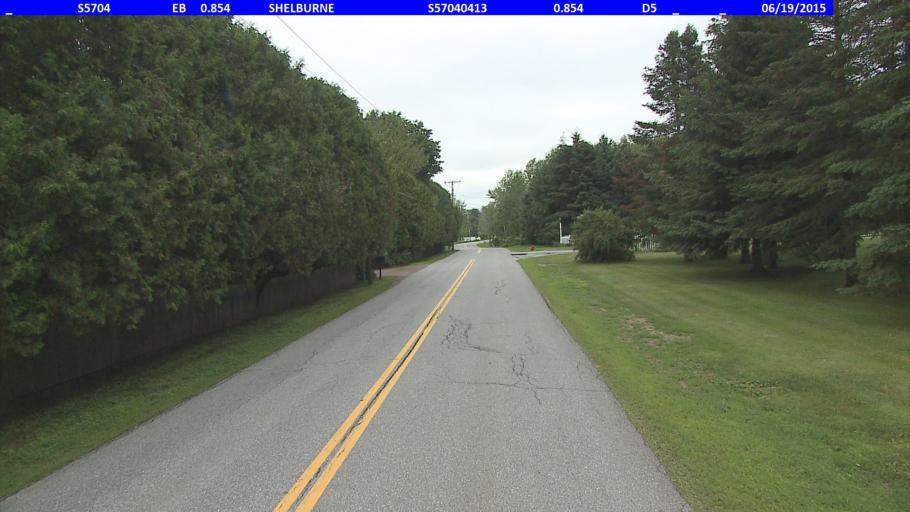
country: US
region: Vermont
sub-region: Chittenden County
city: Burlington
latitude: 44.3990
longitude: -73.2311
